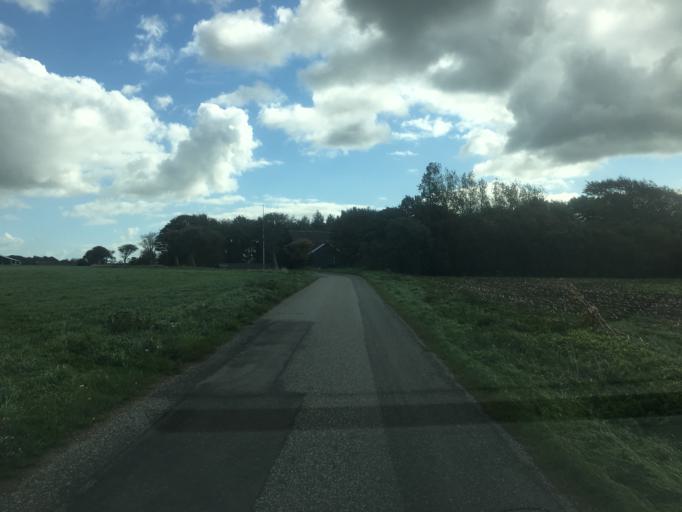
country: DK
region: South Denmark
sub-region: Tonder Kommune
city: Logumkloster
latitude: 55.1162
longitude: 8.8663
